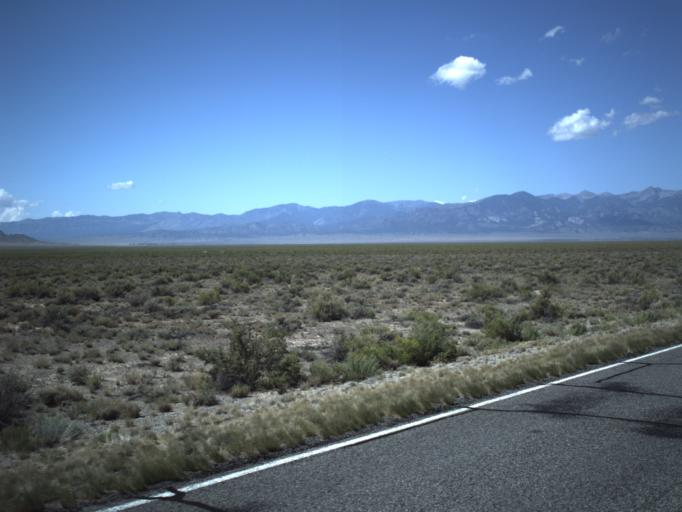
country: US
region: Nevada
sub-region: White Pine County
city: McGill
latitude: 39.0448
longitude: -113.8880
